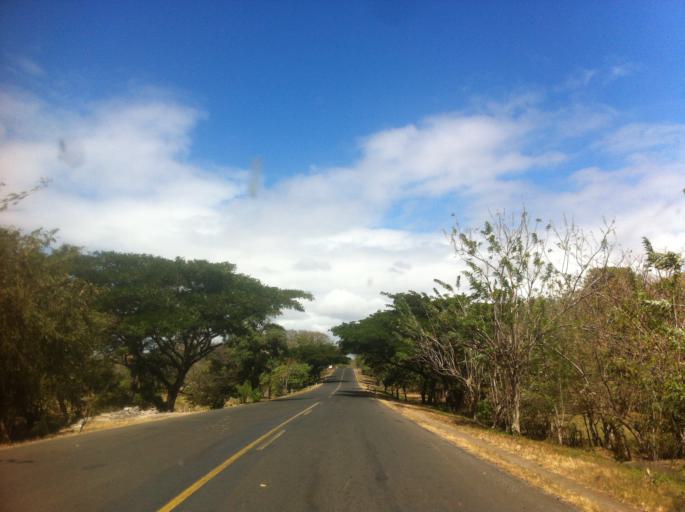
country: NI
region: Chontales
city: Acoyapa
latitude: 12.0103
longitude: -85.2412
